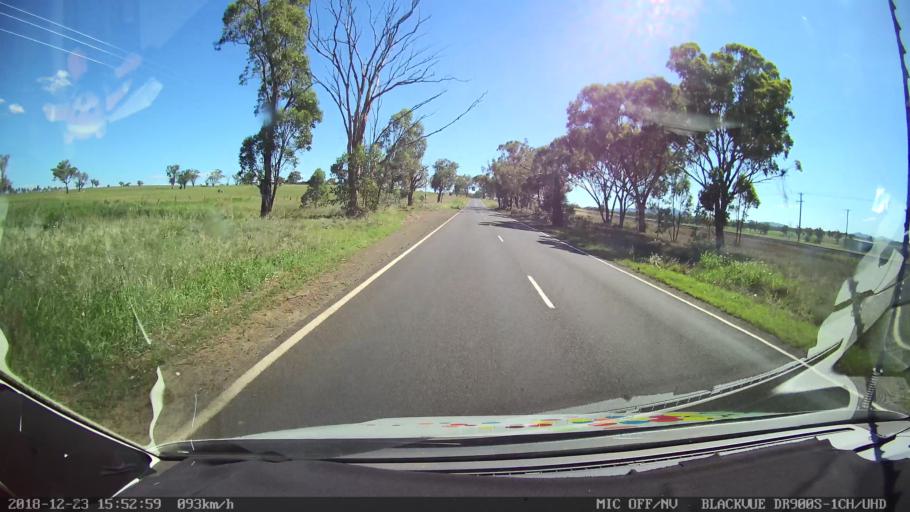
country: AU
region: New South Wales
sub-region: Tamworth Municipality
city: Phillip
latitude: -31.1277
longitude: 150.8846
